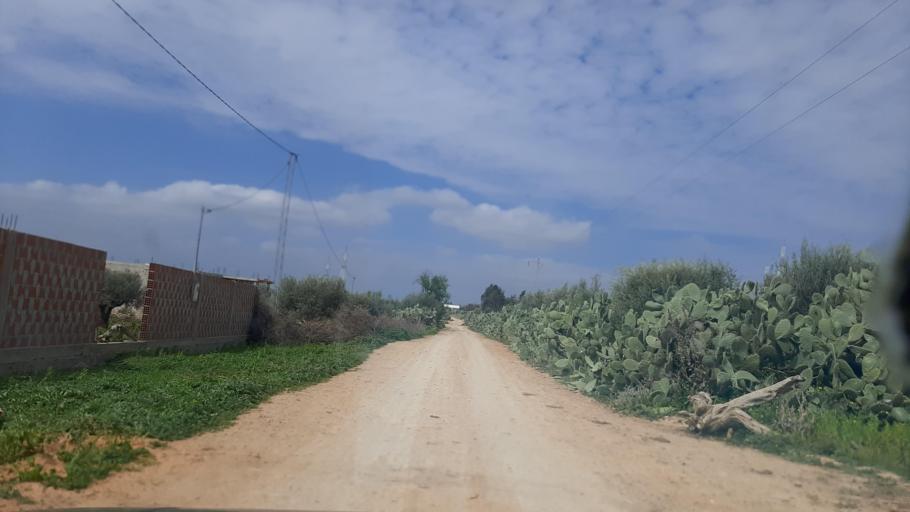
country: TN
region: Tunis
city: La Mohammedia
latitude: 36.6841
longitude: 10.0132
